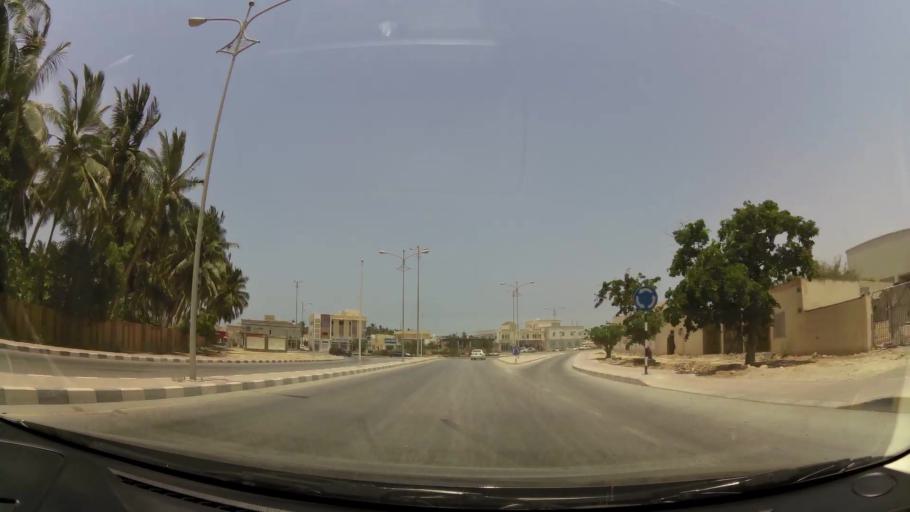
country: OM
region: Zufar
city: Salalah
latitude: 17.0223
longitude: 54.1202
